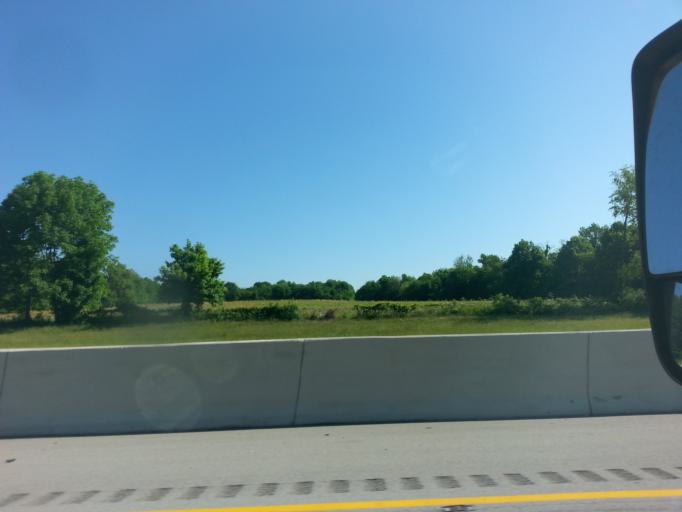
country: US
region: Kentucky
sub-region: Shelby County
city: Simpsonville
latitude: 38.2143
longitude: -85.3851
